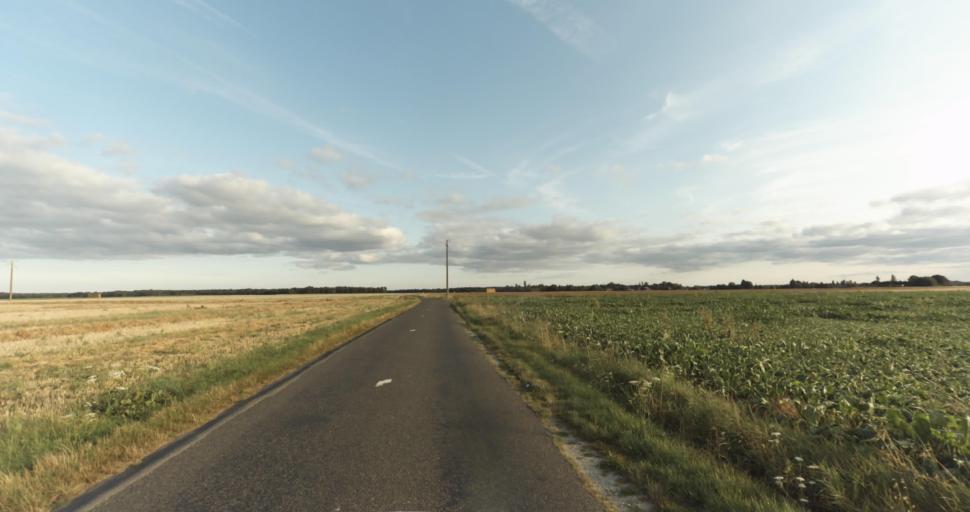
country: FR
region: Haute-Normandie
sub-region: Departement de l'Eure
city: Marcilly-sur-Eure
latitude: 48.8274
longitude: 1.2874
